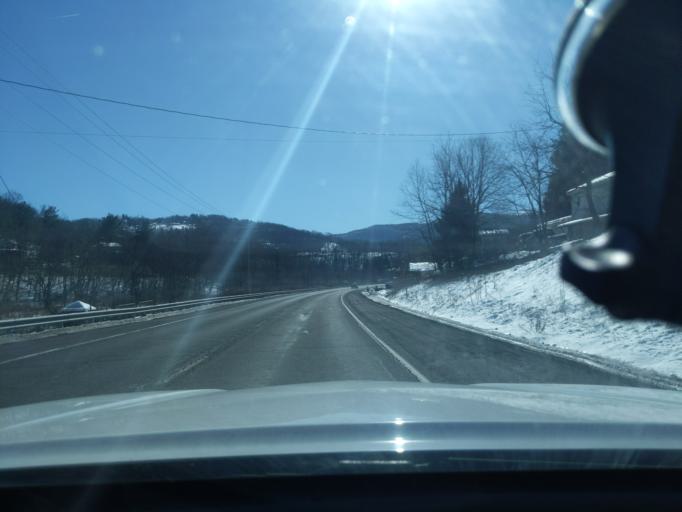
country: US
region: Maryland
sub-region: Allegany County
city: Westernport
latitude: 39.4944
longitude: -79.0451
